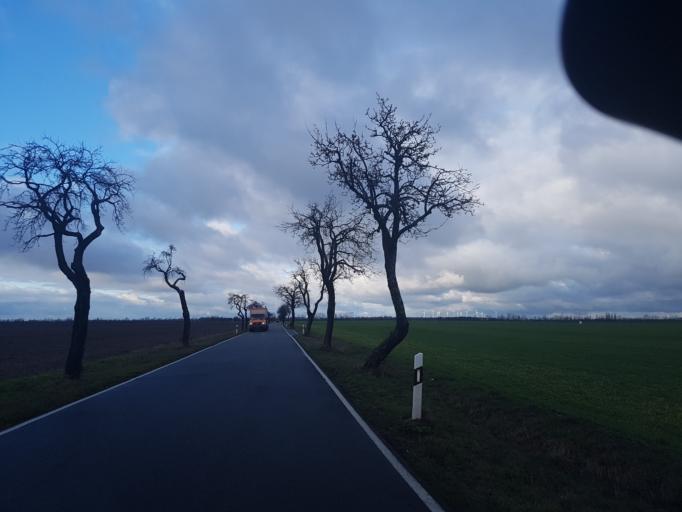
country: DE
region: Brandenburg
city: Muhlberg
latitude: 51.4049
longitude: 13.2418
